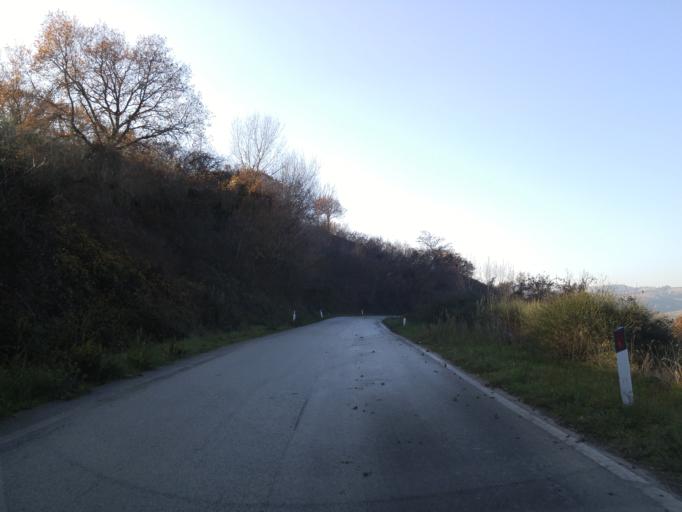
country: IT
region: The Marches
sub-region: Provincia di Pesaro e Urbino
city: Montefelcino
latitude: 43.7465
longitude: 12.8227
